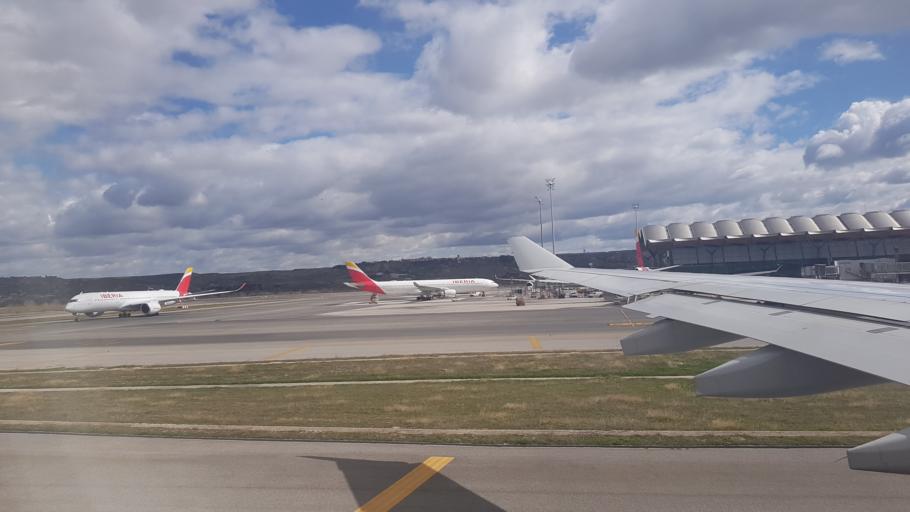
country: ES
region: Madrid
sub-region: Provincia de Madrid
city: Barajas de Madrid
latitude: 40.4989
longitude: -3.5712
